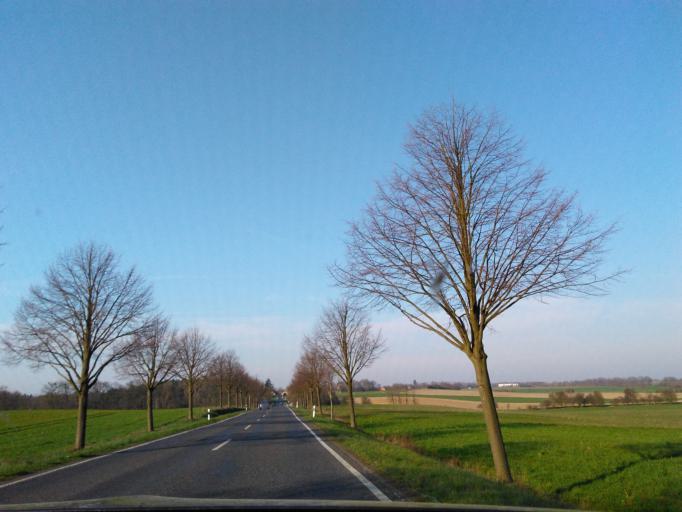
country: DE
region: Brandenburg
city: Protzel
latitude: 52.5737
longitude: 14.0031
